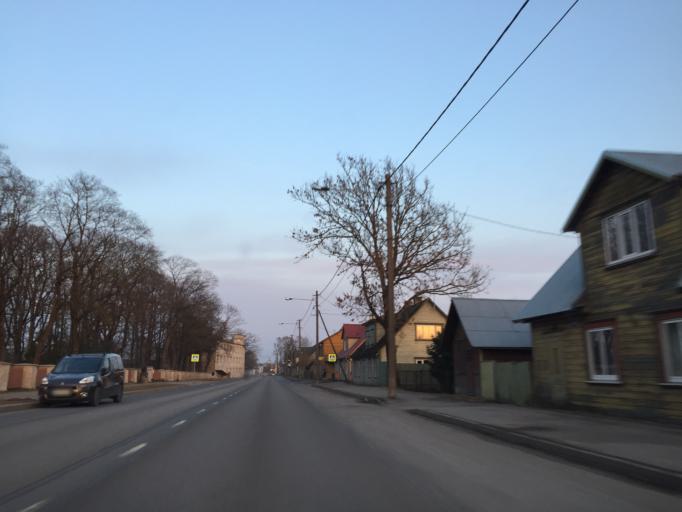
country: EE
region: Paernumaa
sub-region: Paernu linn
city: Parnu
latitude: 58.3893
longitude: 24.4725
